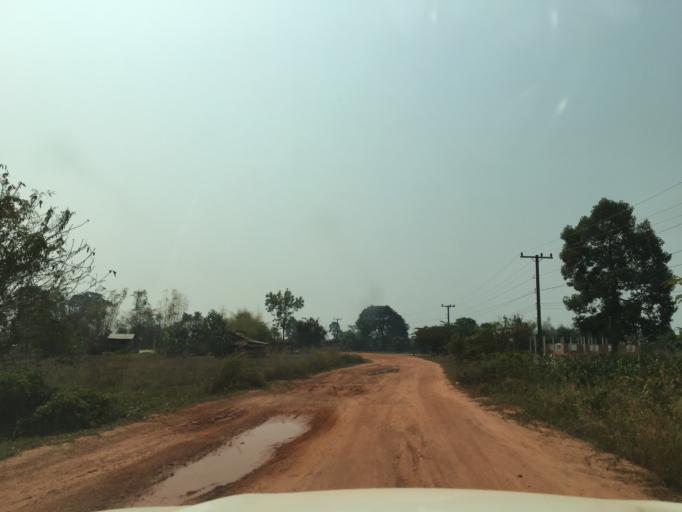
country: TH
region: Changwat Bueng Kan
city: Bung Khla
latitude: 18.2128
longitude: 104.0725
